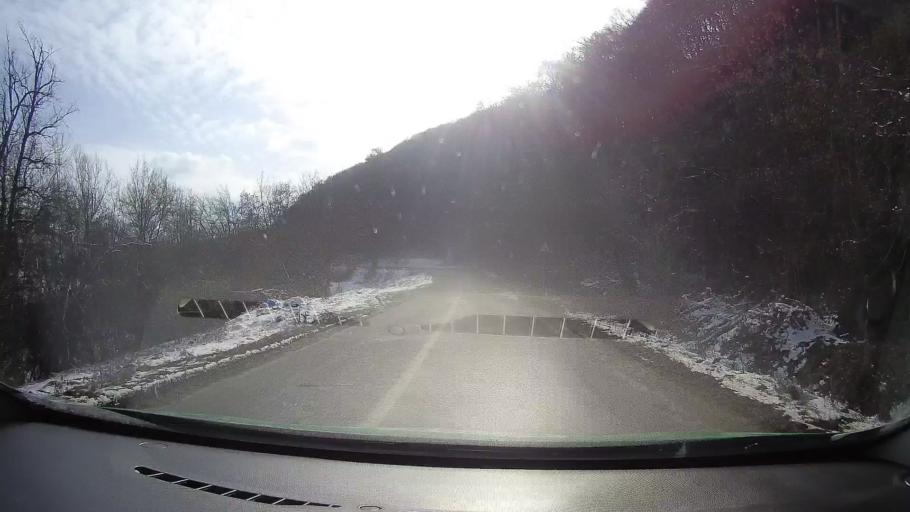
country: RO
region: Mures
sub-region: Comuna Apold
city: Saes
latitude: 46.1802
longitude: 24.7581
